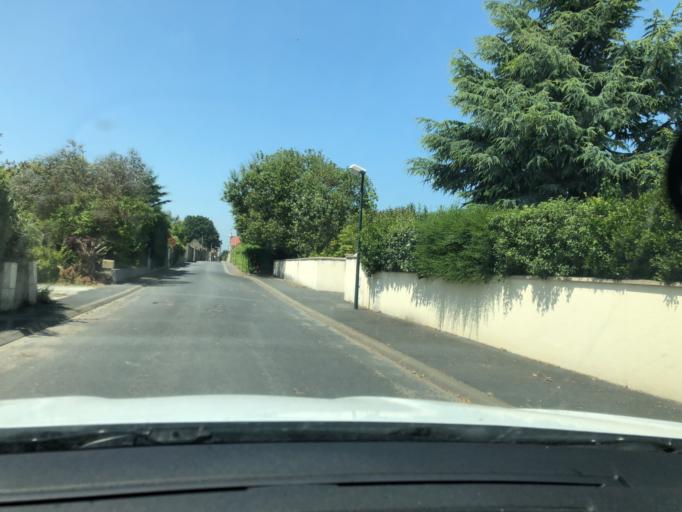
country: FR
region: Lower Normandy
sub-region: Departement du Calvados
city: Lion-sur-Mer
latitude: 49.3033
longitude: -0.3285
